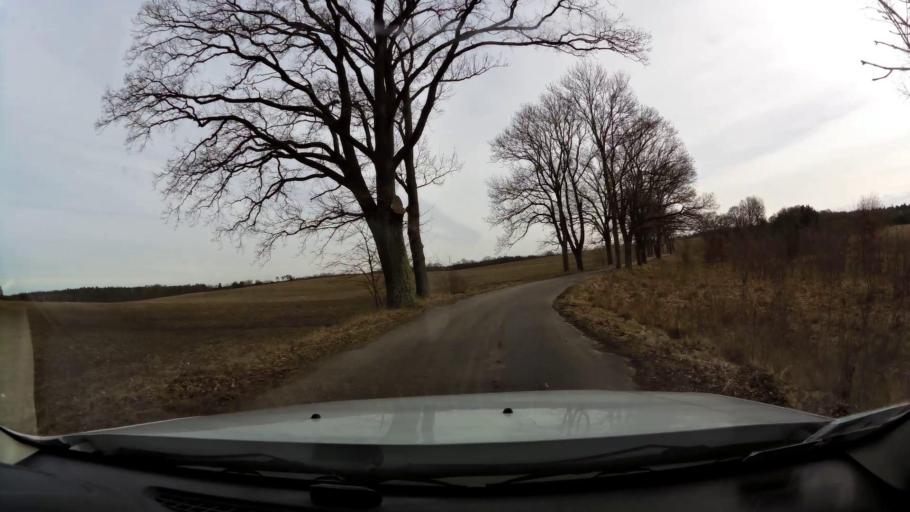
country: PL
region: West Pomeranian Voivodeship
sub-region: Powiat stargardzki
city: Insko
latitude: 53.4538
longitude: 15.6324
